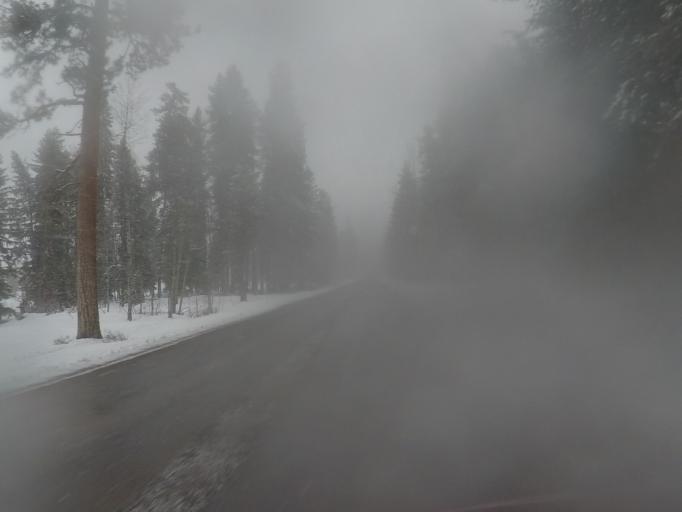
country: US
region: Montana
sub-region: Missoula County
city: Seeley Lake
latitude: 47.4311
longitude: -113.6663
